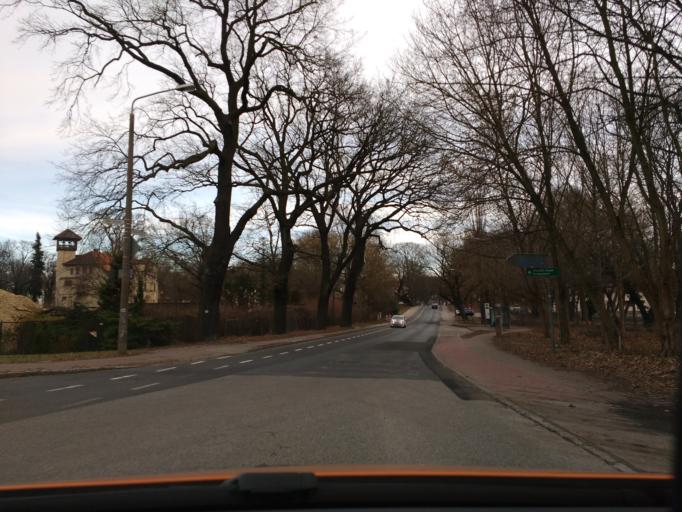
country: DE
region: Brandenburg
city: Potsdam
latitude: 52.3827
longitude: 13.0449
